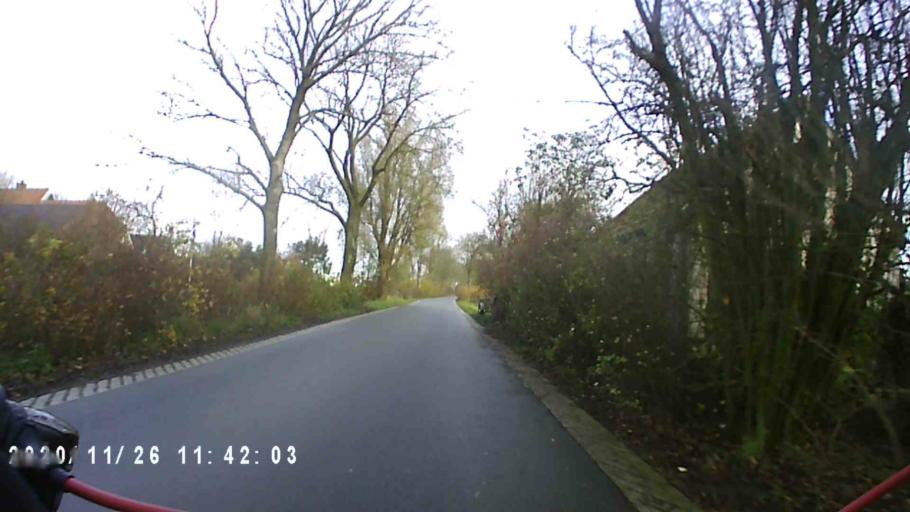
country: NL
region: Groningen
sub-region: Gemeente Bedum
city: Bedum
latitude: 53.2933
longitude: 6.5727
